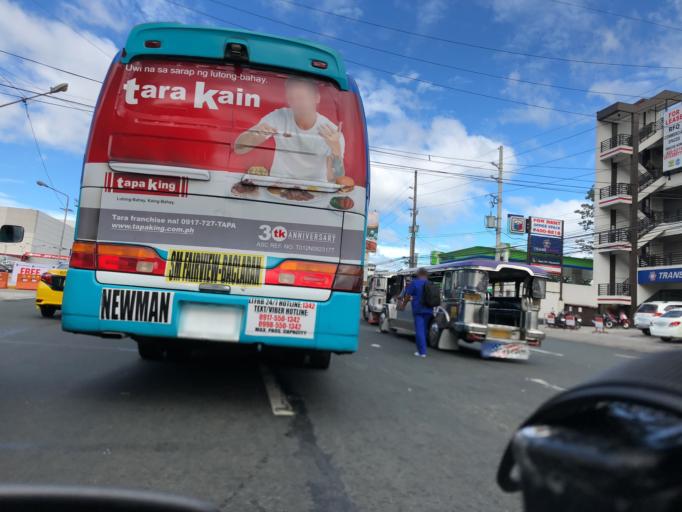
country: PH
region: Calabarzon
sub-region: Province of Rizal
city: San Mateo
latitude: 14.7316
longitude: 121.0612
